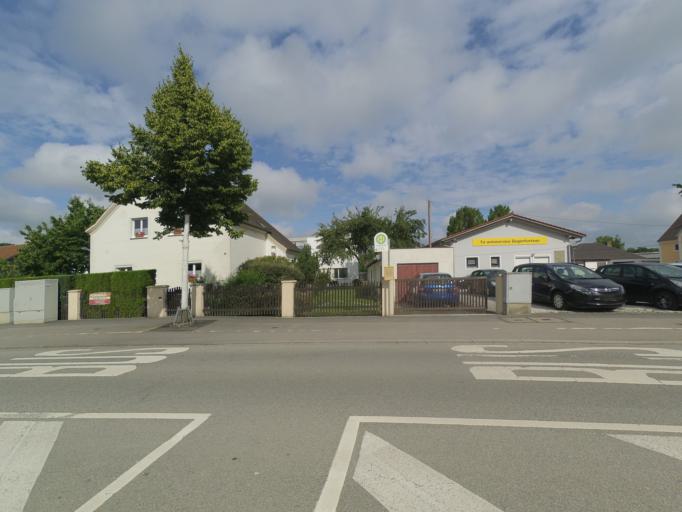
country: DE
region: Bavaria
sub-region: Lower Bavaria
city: Straubing
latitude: 48.8892
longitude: 12.5756
